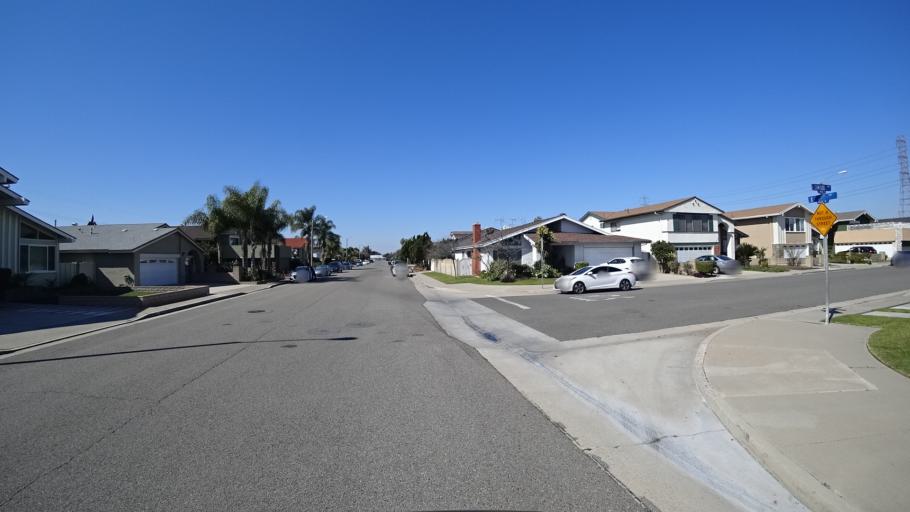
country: US
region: California
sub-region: Orange County
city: Garden Grove
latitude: 33.8054
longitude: -117.9382
